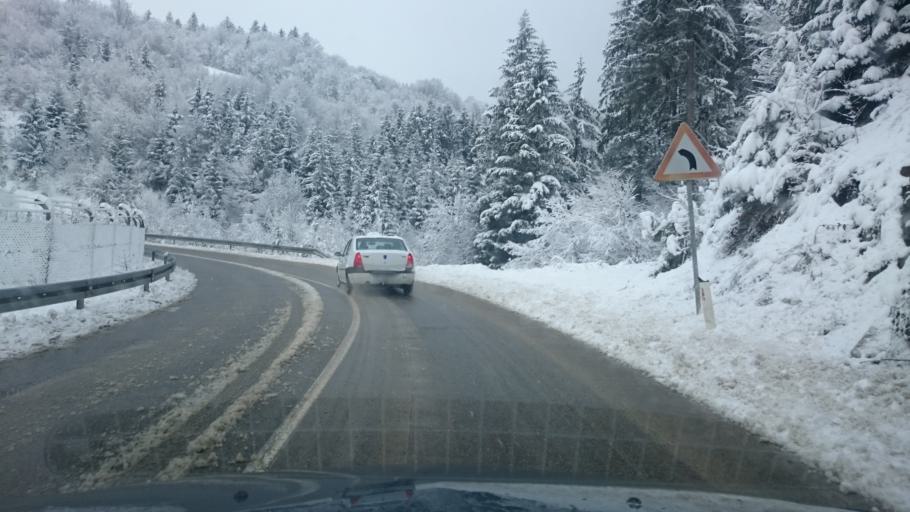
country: BA
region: Republika Srpska
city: Skender Vakuf
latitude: 44.4791
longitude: 17.3901
